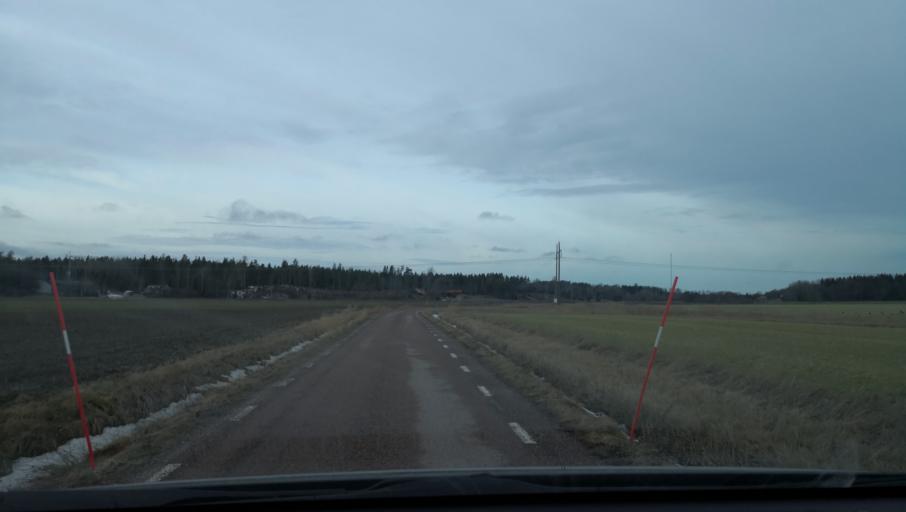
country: SE
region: Vaestmanland
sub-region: Vasteras
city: Skultuna
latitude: 59.5986
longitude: 16.4142
